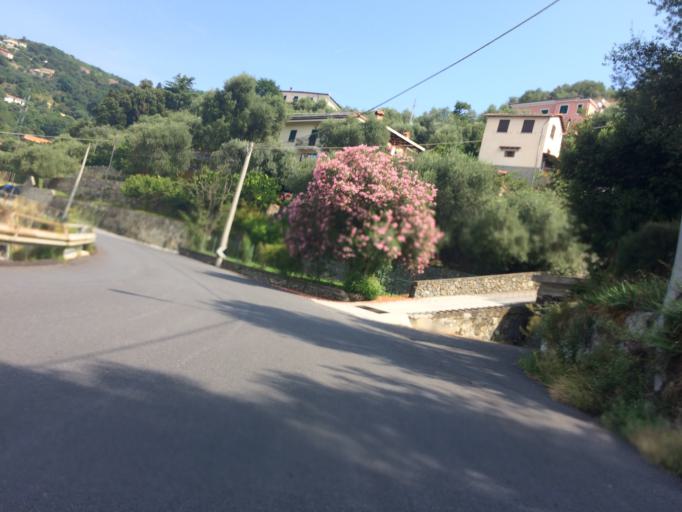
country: IT
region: Liguria
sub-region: Provincia di Savona
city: Varazze
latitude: 44.3753
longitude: 8.5762
